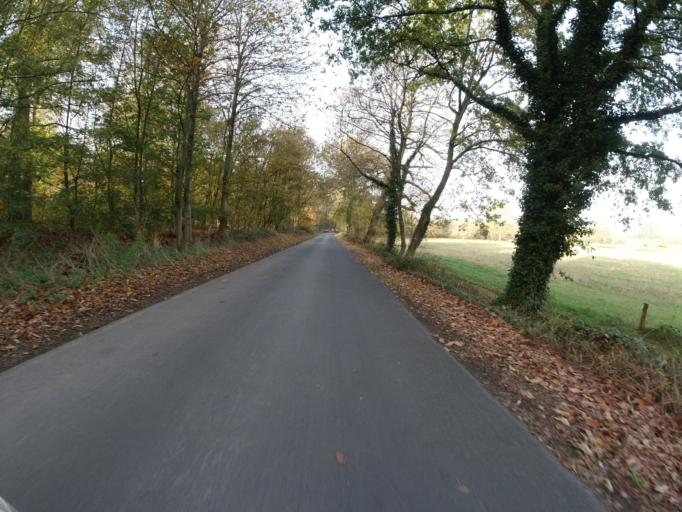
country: DE
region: North Rhine-Westphalia
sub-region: Regierungsbezirk Dusseldorf
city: Moers
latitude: 51.4045
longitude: 6.6293
